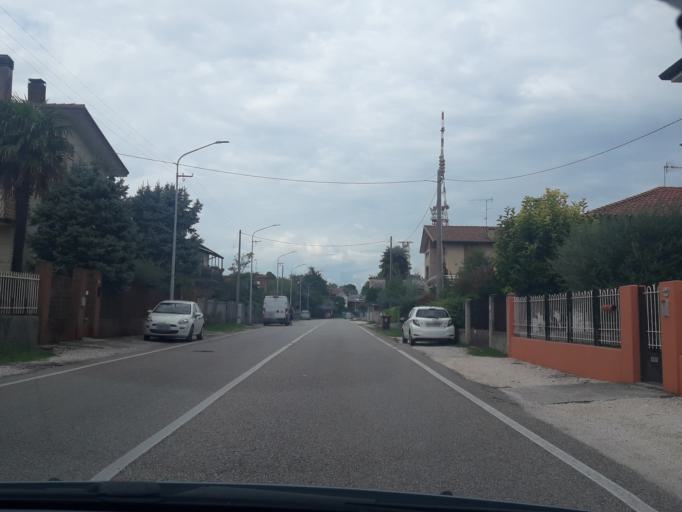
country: IT
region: Friuli Venezia Giulia
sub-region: Provincia di Udine
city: Udine
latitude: 46.0345
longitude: 13.2582
